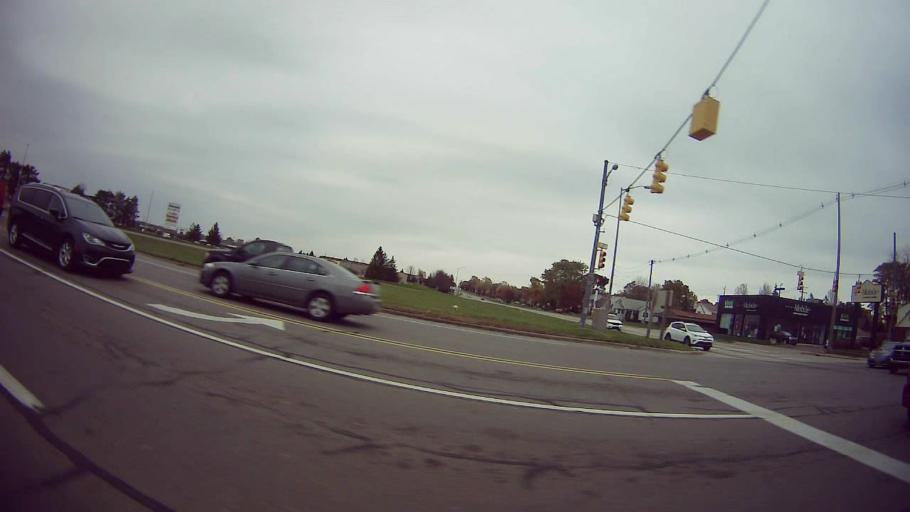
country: US
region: Michigan
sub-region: Oakland County
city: Sylvan Lake
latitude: 42.6402
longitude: -83.3260
